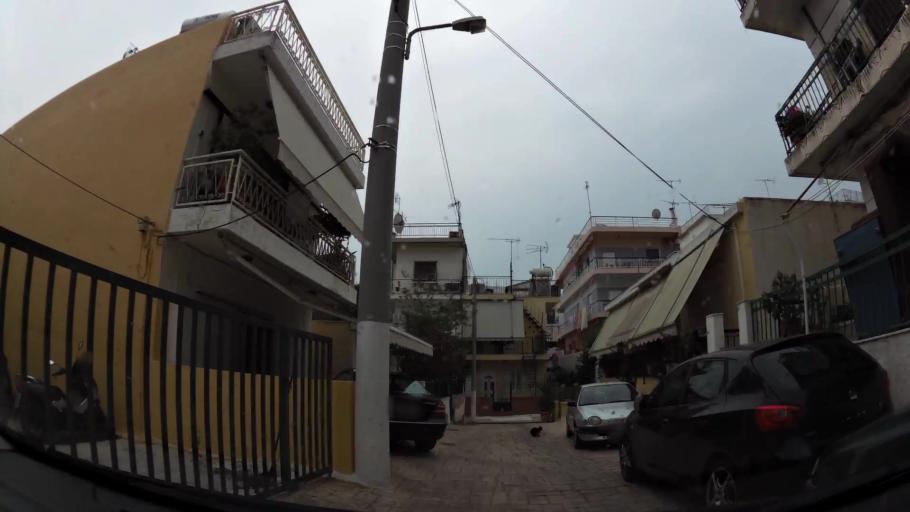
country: GR
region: Attica
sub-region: Nomarchia Athinas
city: Chaidari
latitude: 38.0065
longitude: 23.6653
